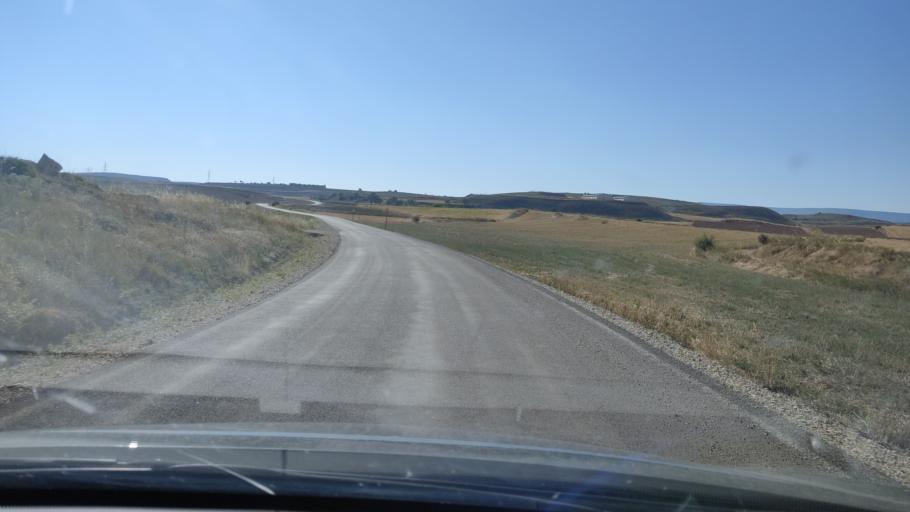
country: ES
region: Aragon
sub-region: Provincia de Teruel
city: Monforte de Moyuela
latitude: 41.0458
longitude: -1.0034
